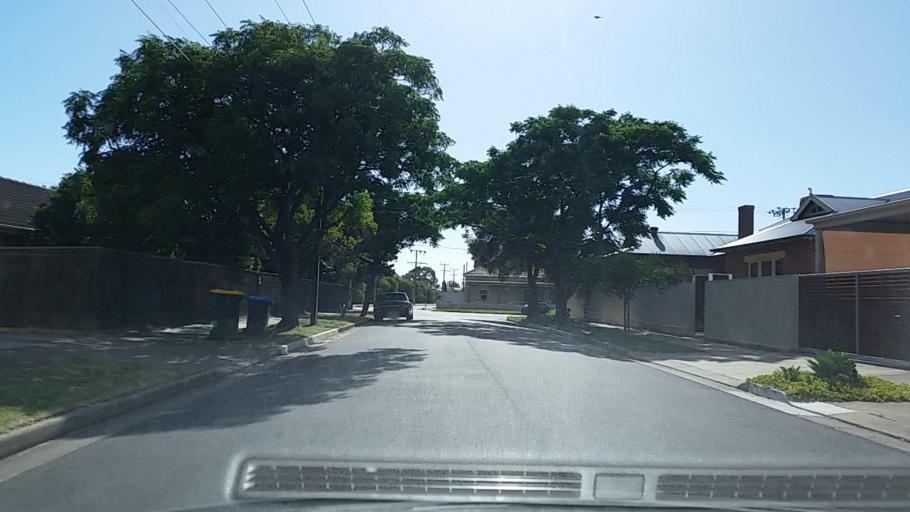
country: AU
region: South Australia
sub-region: Charles Sturt
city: Allenby Gardens
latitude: -34.8966
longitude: 138.5523
